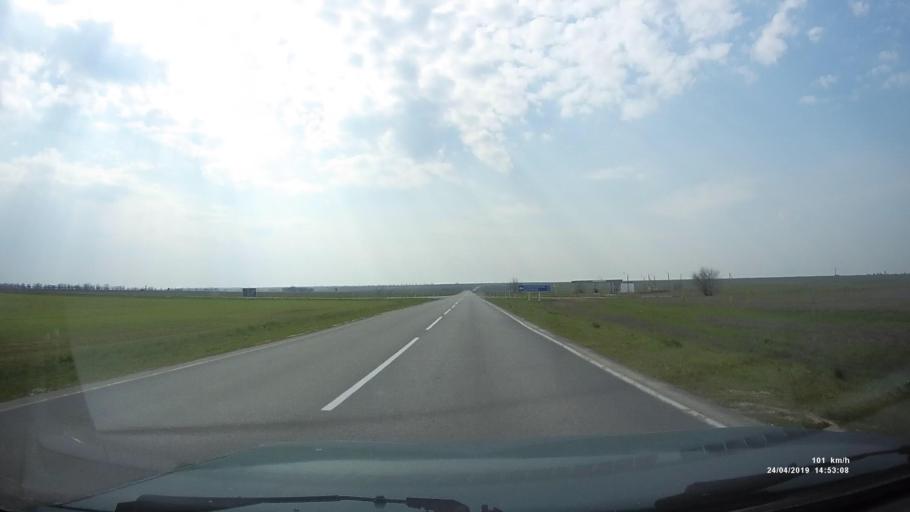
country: RU
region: Rostov
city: Remontnoye
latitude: 46.5309
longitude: 43.6655
